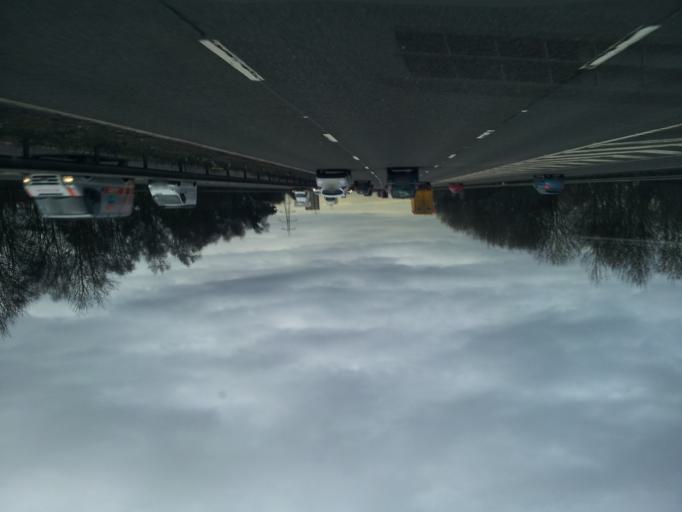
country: GB
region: England
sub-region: Warwickshire
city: Exhall
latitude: 52.4610
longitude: -1.4883
